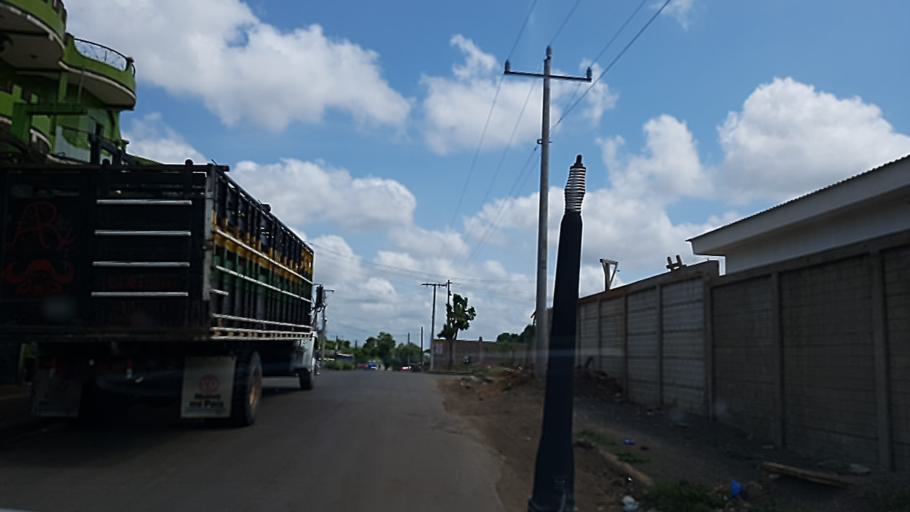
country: NI
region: Atlantico Sur
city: Nueva Guinea
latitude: 11.6861
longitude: -84.4606
